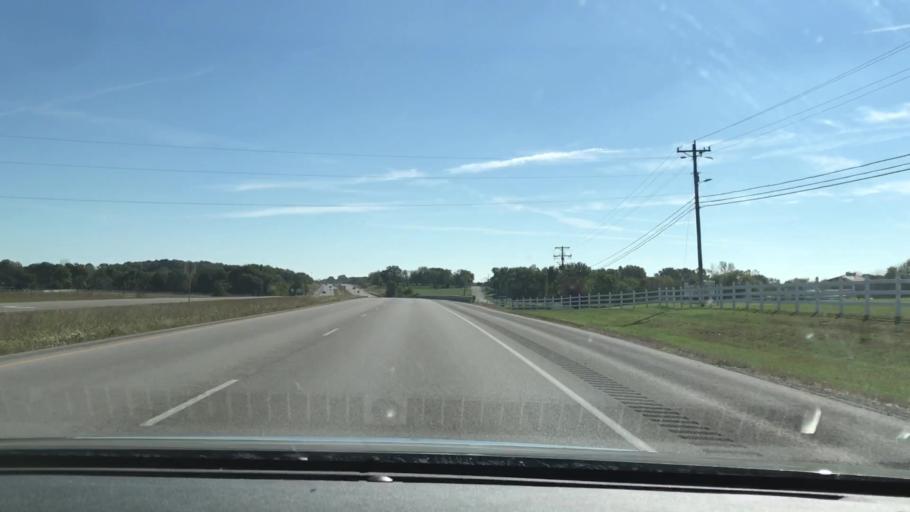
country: US
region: Kentucky
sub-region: Christian County
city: Hopkinsville
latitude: 36.8568
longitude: -87.4228
